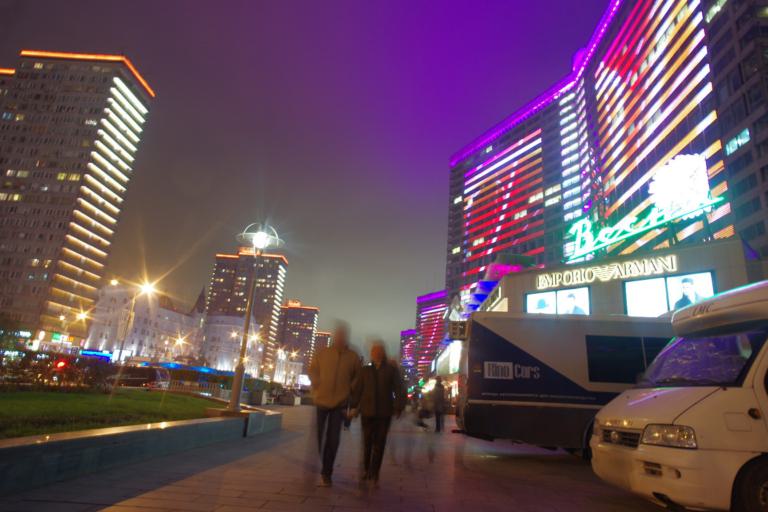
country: RU
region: Moskovskaya
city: Dorogomilovo
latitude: 55.7522
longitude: 37.5871
